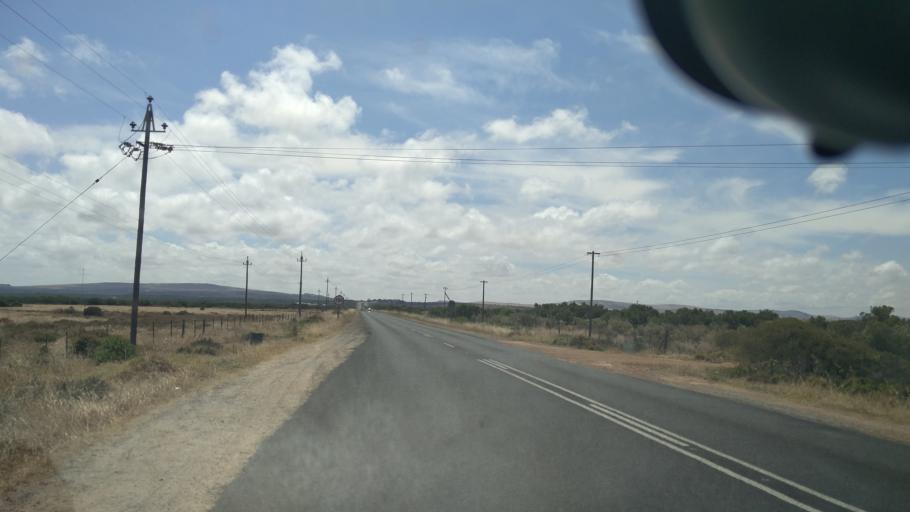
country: ZA
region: Western Cape
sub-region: City of Cape Town
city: Atlantis
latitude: -33.3420
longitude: 18.1767
